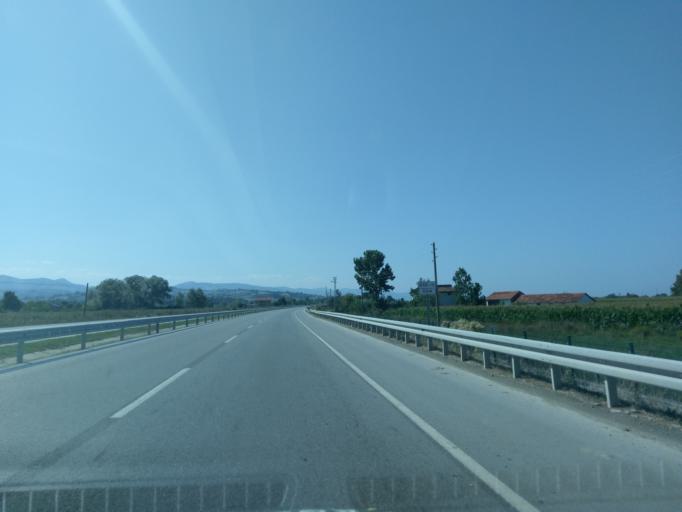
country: TR
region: Samsun
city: Alacam
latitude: 41.6084
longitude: 35.6685
